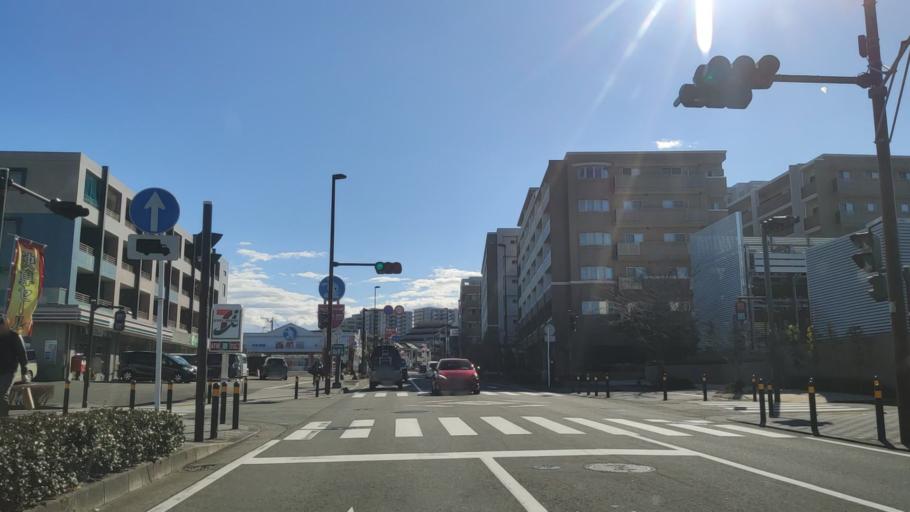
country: JP
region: Tokyo
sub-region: Machida-shi
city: Machida
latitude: 35.5246
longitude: 139.4984
